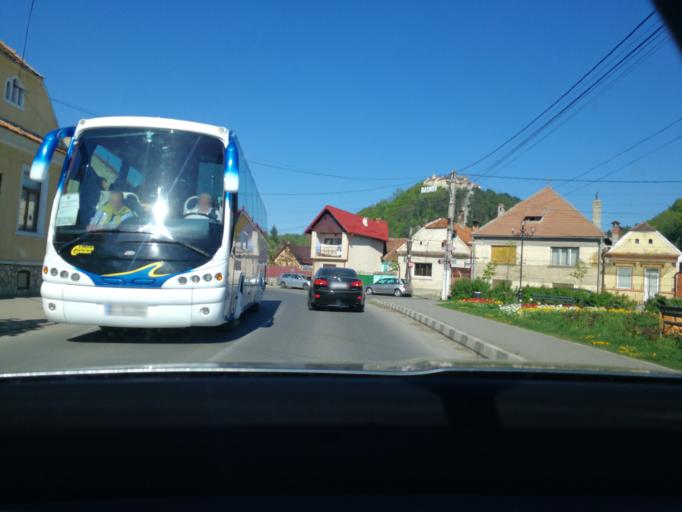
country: RO
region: Brasov
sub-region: Oras Rasnov
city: Rasnov
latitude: 45.5896
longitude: 25.4600
